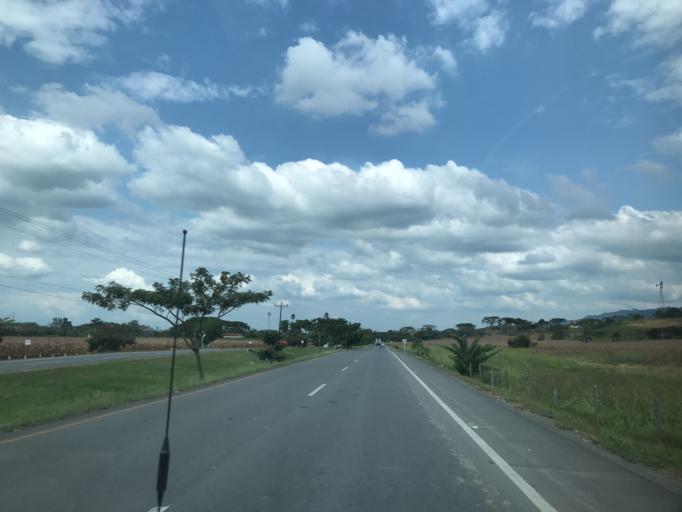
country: CO
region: Valle del Cauca
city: Obando
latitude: 4.5873
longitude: -75.9692
